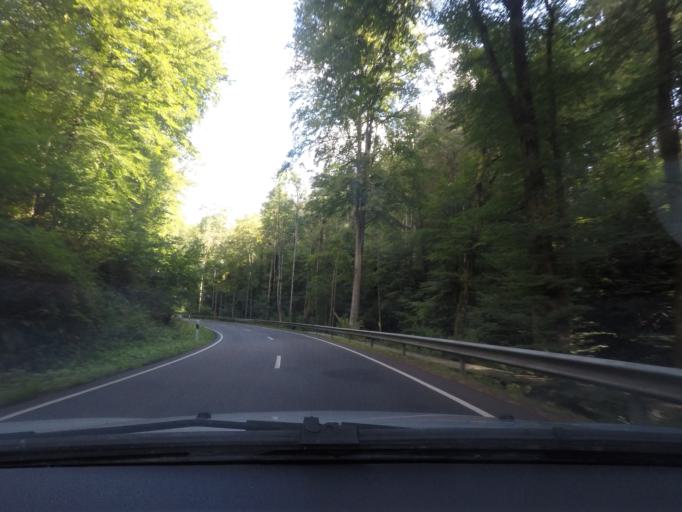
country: LU
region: Grevenmacher
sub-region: Canton d'Echternach
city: Waldbillig
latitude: 49.7669
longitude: 6.2836
